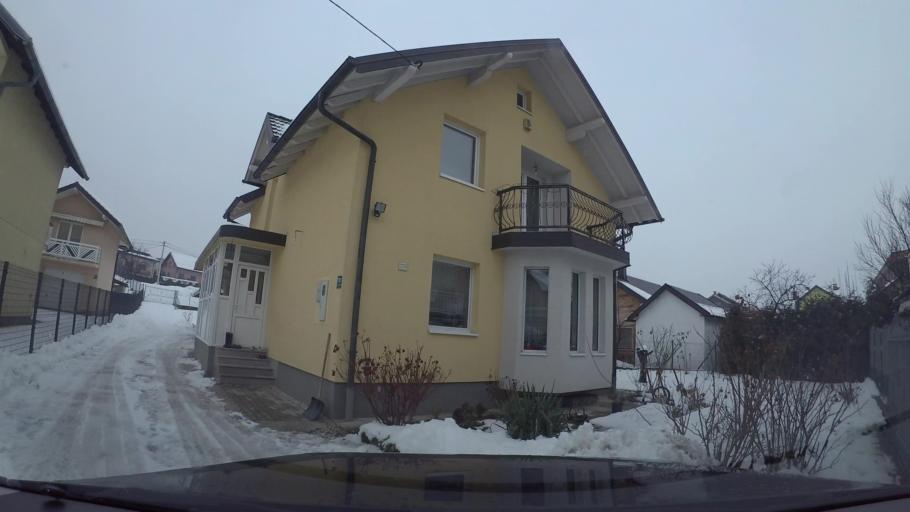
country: BA
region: Federation of Bosnia and Herzegovina
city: Hadzici
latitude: 43.8466
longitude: 18.2784
